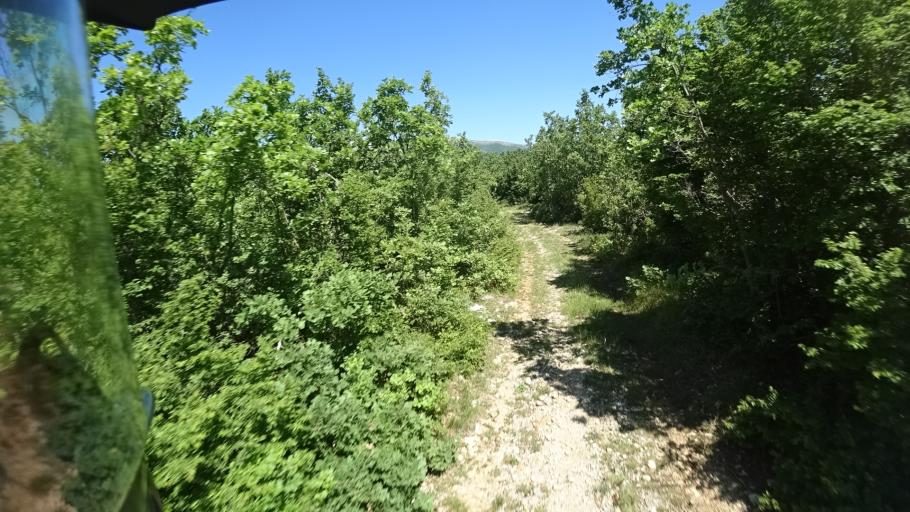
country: BA
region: Federation of Bosnia and Herzegovina
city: Bosansko Grahovo
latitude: 43.9884
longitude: 16.4236
